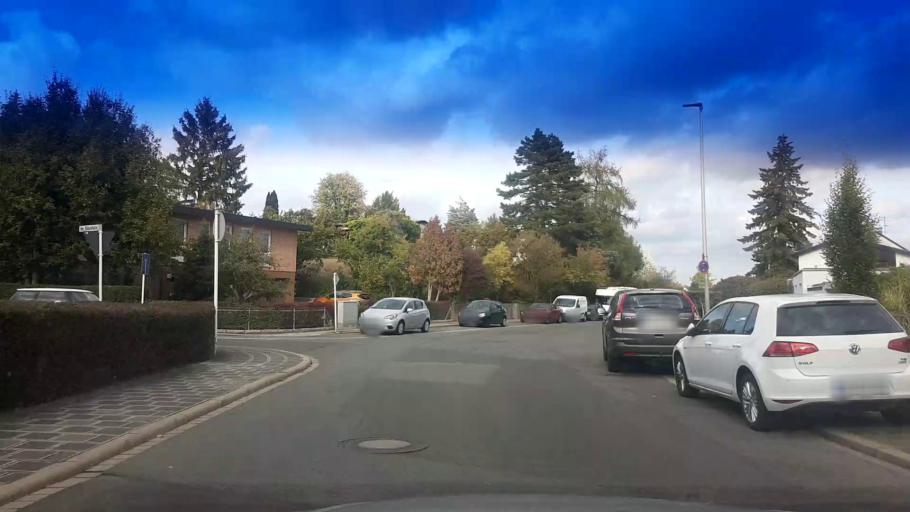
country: DE
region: Bavaria
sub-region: Upper Franconia
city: Bamberg
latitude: 49.8771
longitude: 10.8759
